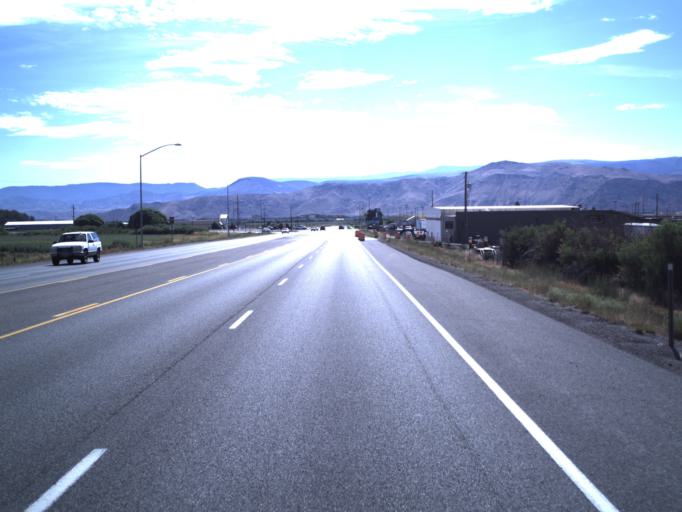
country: US
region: Utah
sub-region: Sevier County
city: Richfield
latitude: 38.7497
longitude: -112.0924
